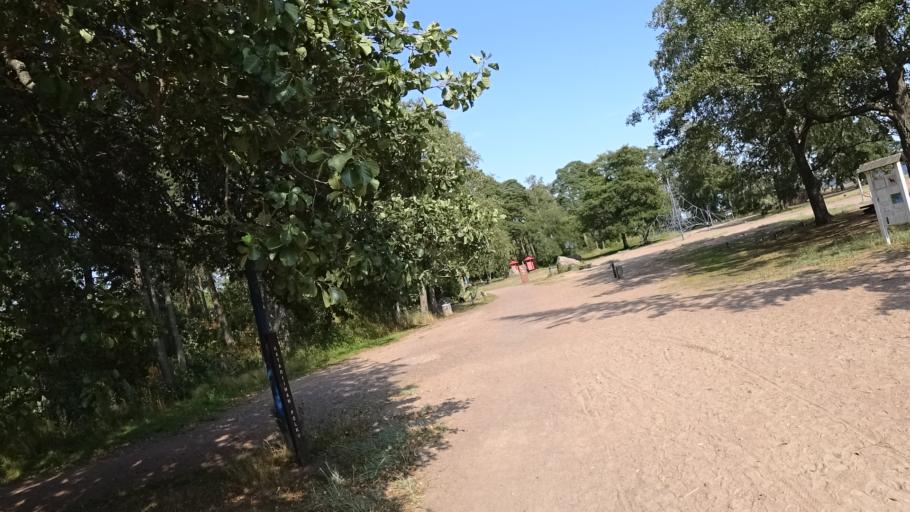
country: FI
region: Kymenlaakso
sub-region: Kotka-Hamina
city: Kotka
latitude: 60.4513
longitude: 26.9462
